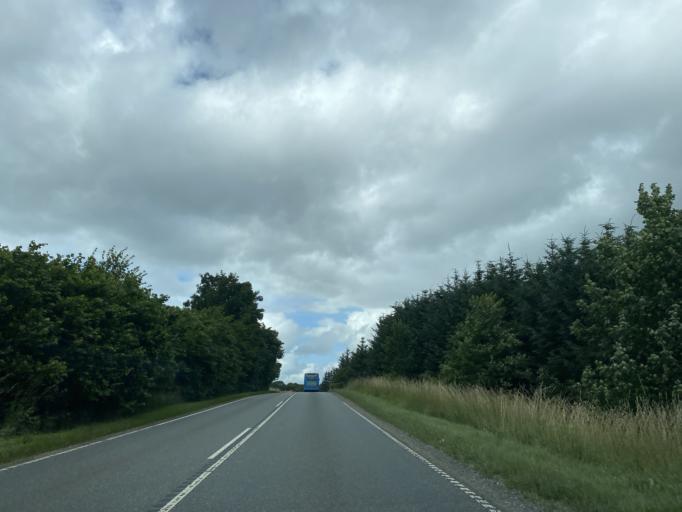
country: DK
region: Central Jutland
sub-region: Silkeborg Kommune
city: Silkeborg
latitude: 56.2479
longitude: 9.6253
